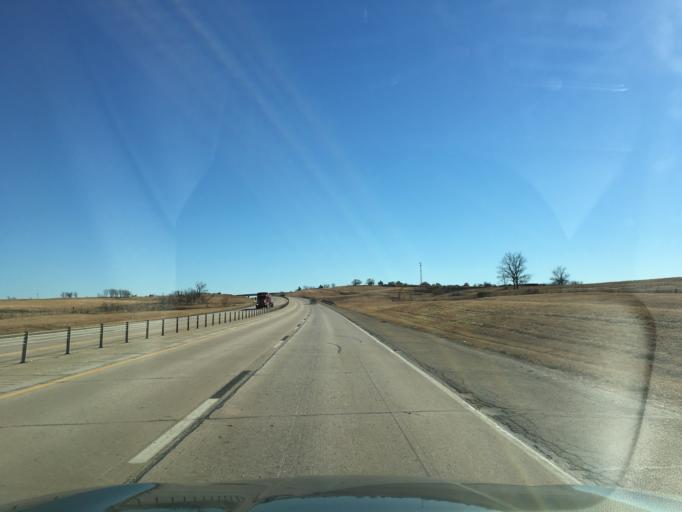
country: US
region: Oklahoma
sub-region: Payne County
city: Stillwater
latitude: 36.2524
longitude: -96.9680
